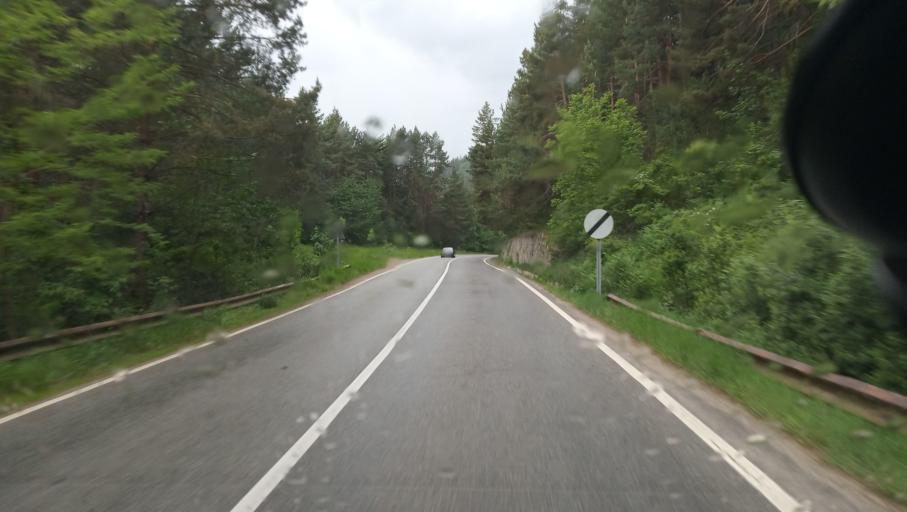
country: RO
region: Neamt
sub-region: Comuna Ceahlau
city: Ceahlau
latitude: 47.0630
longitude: 25.9377
